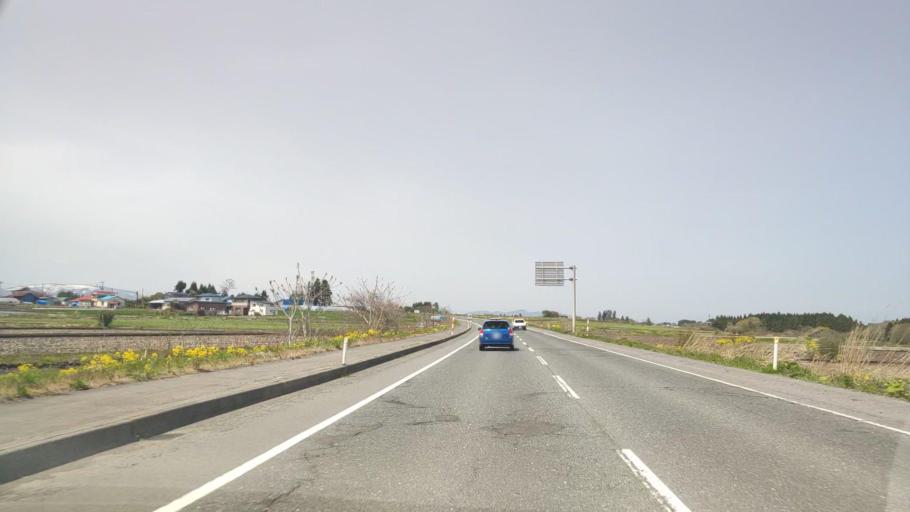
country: JP
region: Aomori
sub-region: Misawa Shi
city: Inuotose
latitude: 40.6349
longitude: 141.2442
